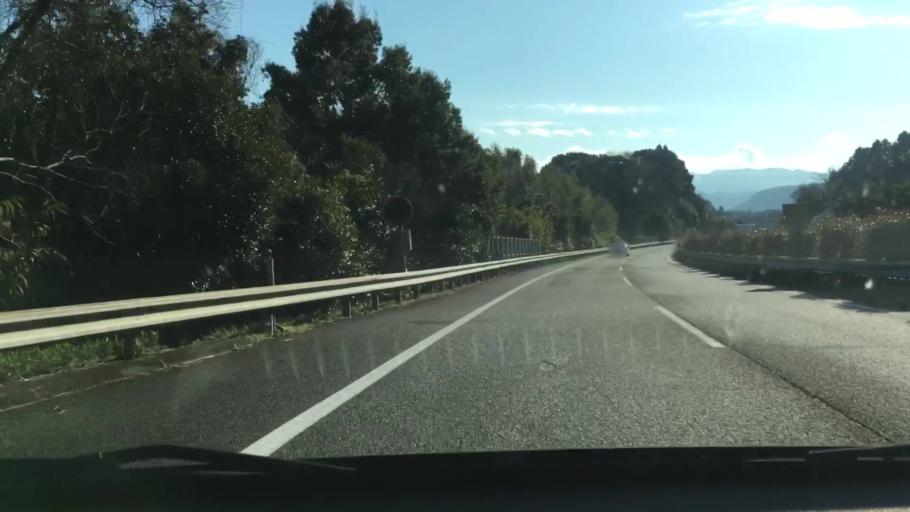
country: JP
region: Kumamoto
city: Hitoyoshi
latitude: 32.2181
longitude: 130.7801
